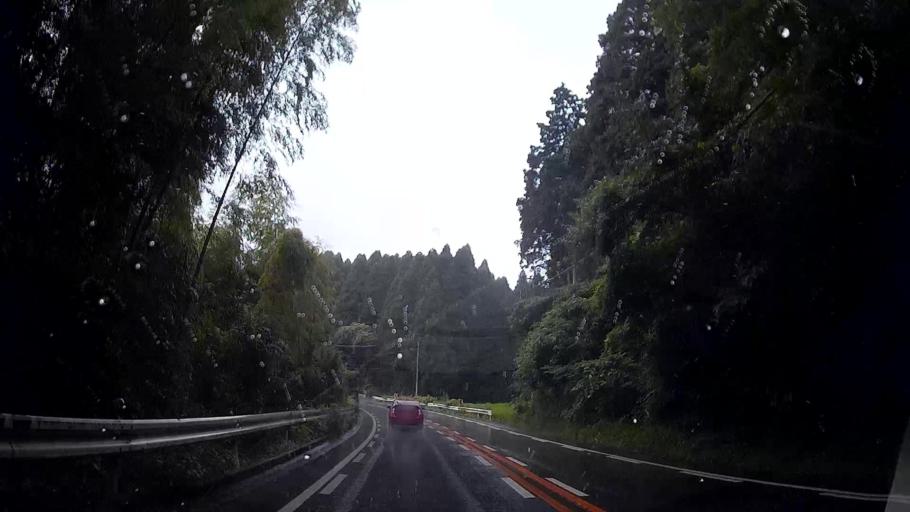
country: JP
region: Kumamoto
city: Aso
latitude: 32.8674
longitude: 131.0001
